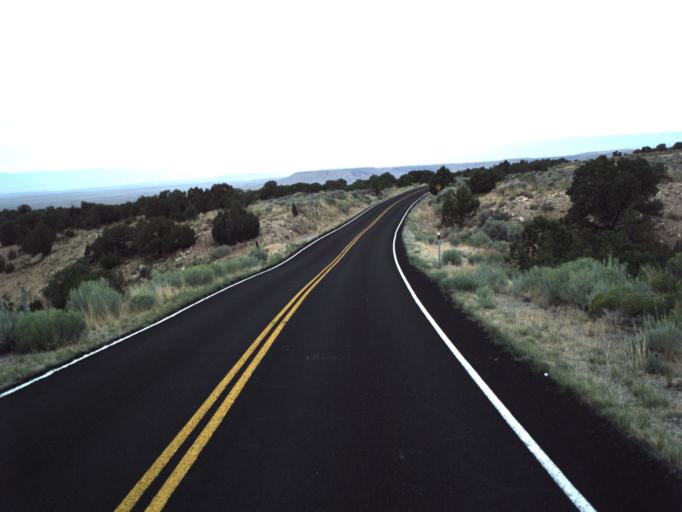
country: US
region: Utah
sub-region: Carbon County
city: East Carbon City
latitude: 39.4542
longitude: -110.3822
